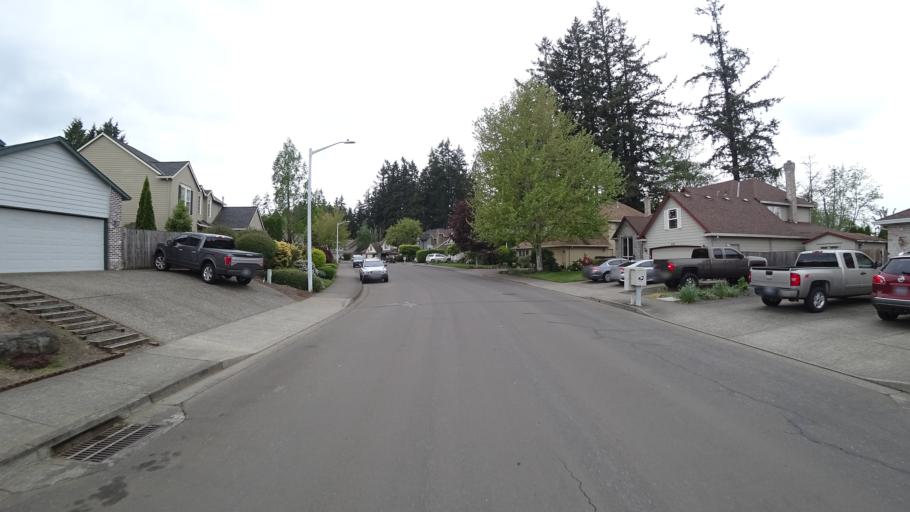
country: US
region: Oregon
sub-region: Washington County
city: Hillsboro
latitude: 45.5429
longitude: -122.9866
